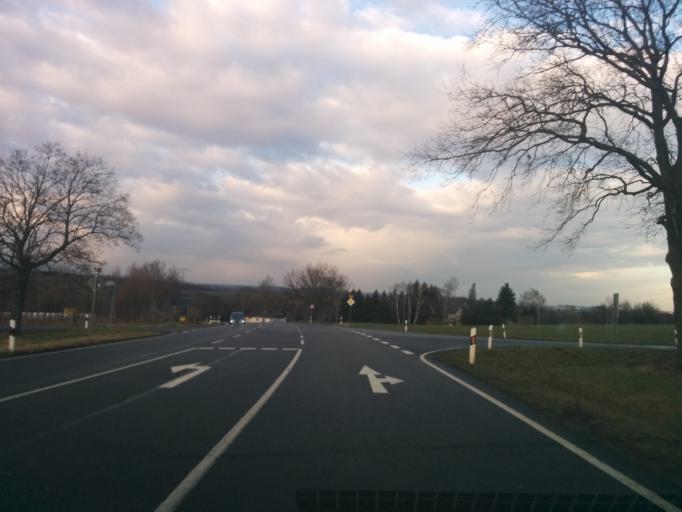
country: DE
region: Saxony
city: Niederwiesa
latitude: 50.8838
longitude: 12.9868
